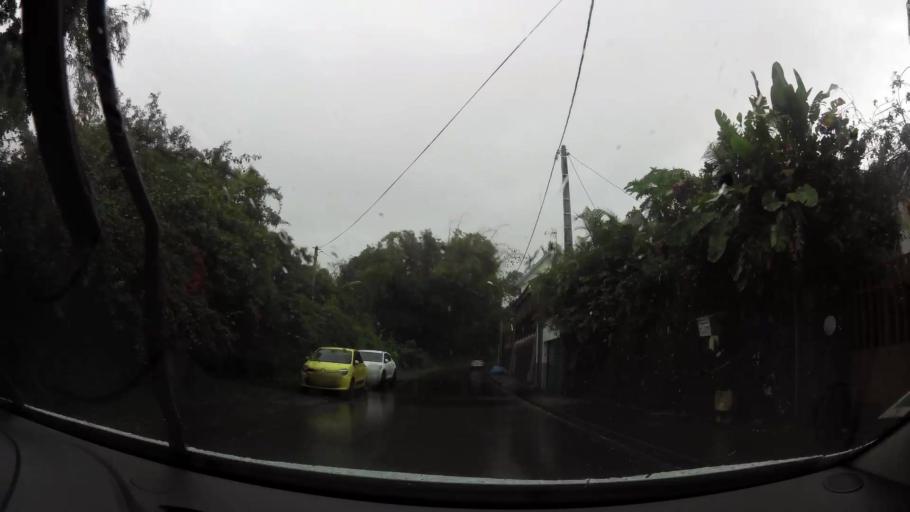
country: RE
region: Reunion
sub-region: Reunion
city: Saint-Andre
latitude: -20.9646
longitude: 55.6486
